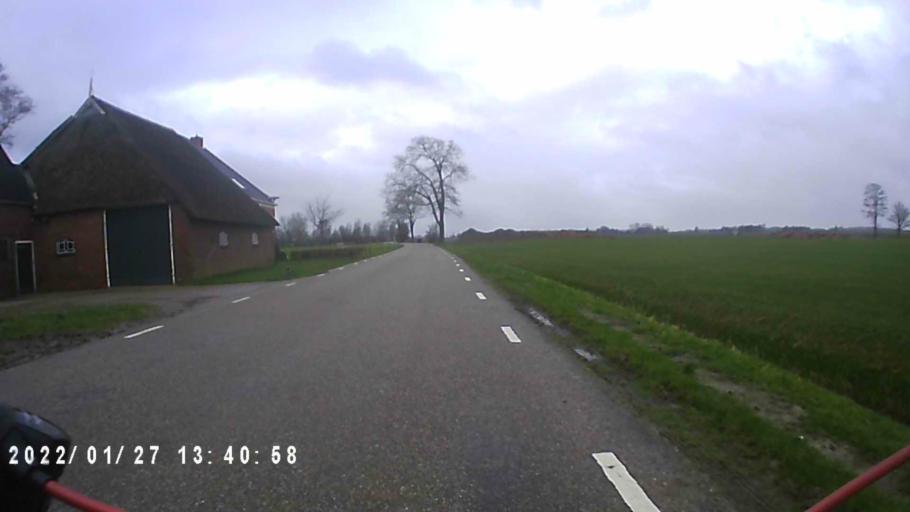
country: NL
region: Friesland
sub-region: Gemeente Kollumerland en Nieuwkruisland
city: Kollum
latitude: 53.3008
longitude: 6.2161
